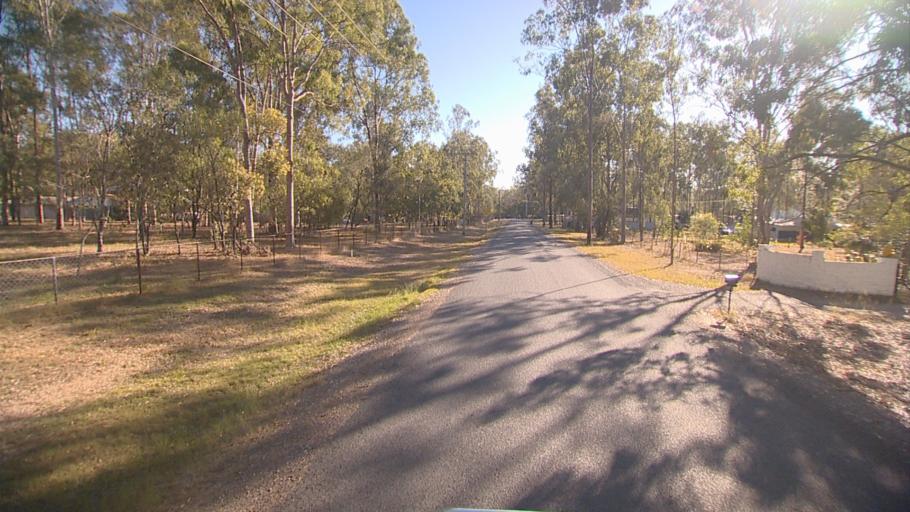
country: AU
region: Queensland
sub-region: Logan
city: North Maclean
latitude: -27.7843
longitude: 152.9853
